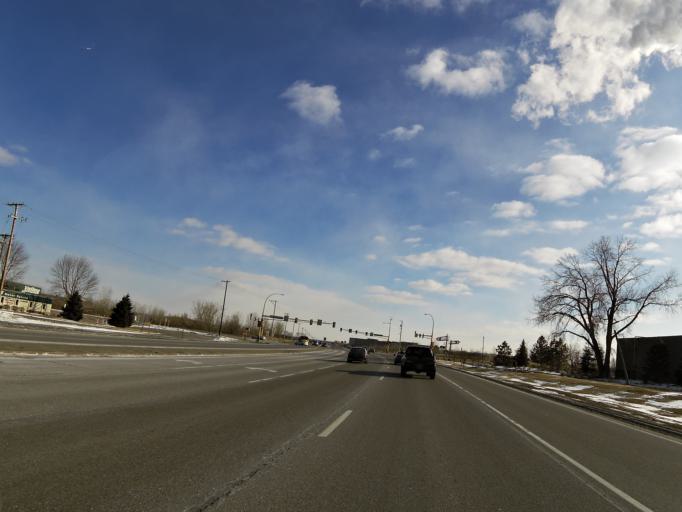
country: US
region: Minnesota
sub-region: Dakota County
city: Mendota Heights
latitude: 44.8351
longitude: -93.1173
